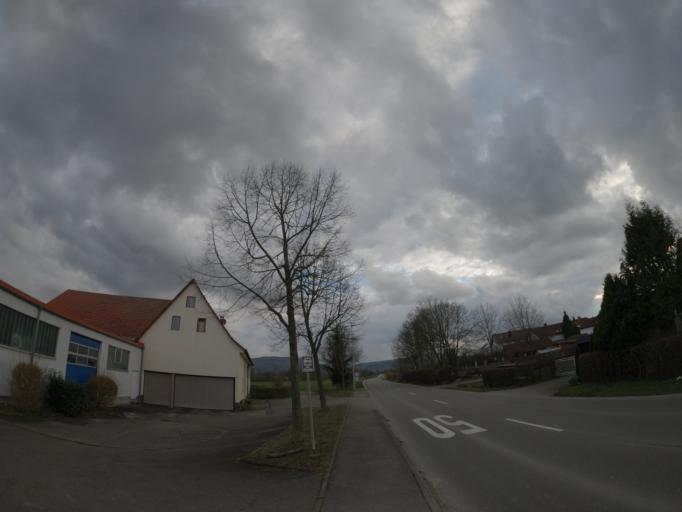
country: DE
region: Baden-Wuerttemberg
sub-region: Regierungsbezirk Stuttgart
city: Boll
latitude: 48.6640
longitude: 9.6147
